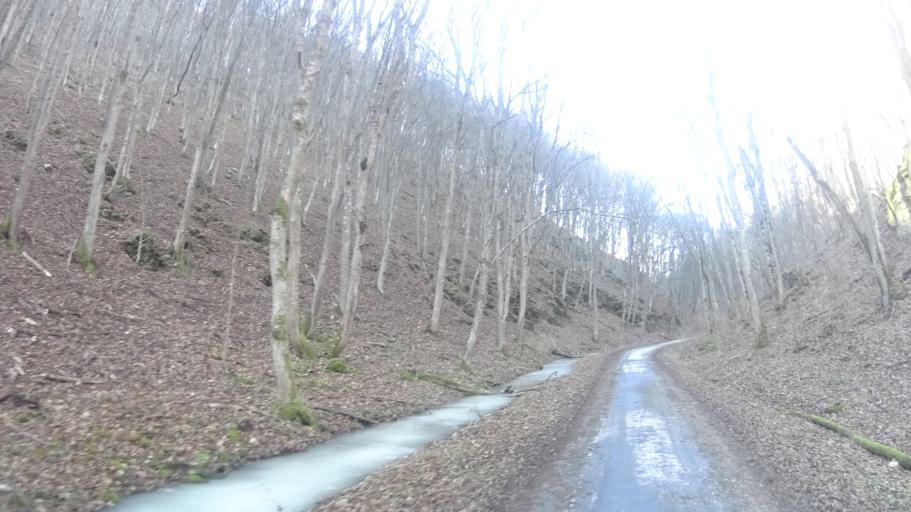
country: HU
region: Borsod-Abauj-Zemplen
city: Bogacs
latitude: 47.9998
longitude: 20.5198
